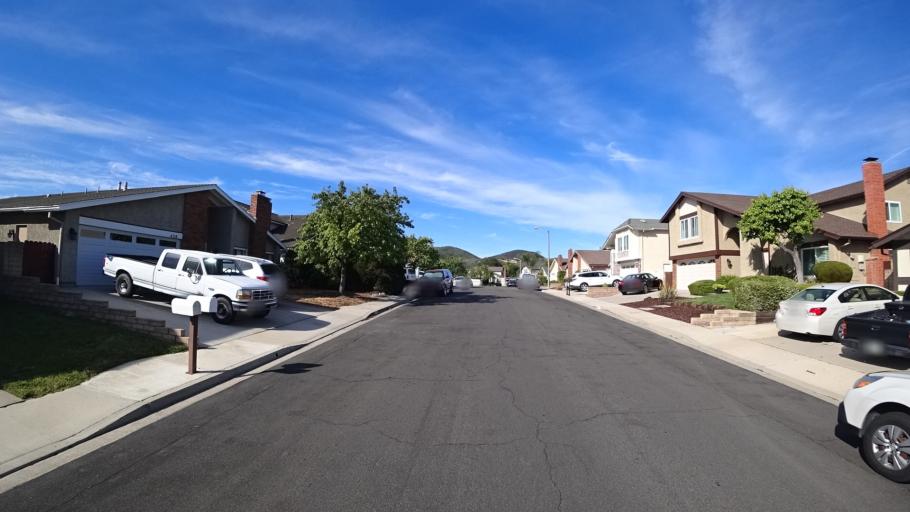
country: US
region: California
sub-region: Ventura County
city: Casa Conejo
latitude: 34.1714
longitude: -118.9594
